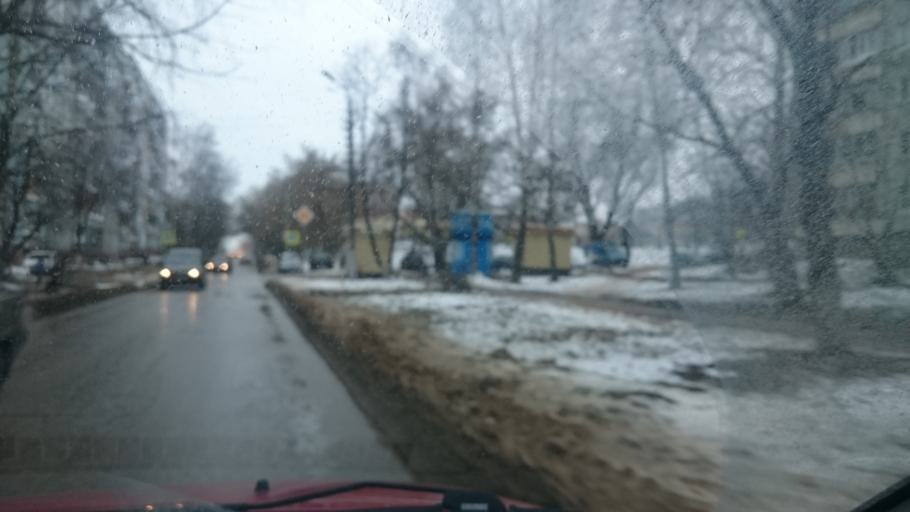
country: RU
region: Tula
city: Tula
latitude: 54.2158
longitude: 37.6301
